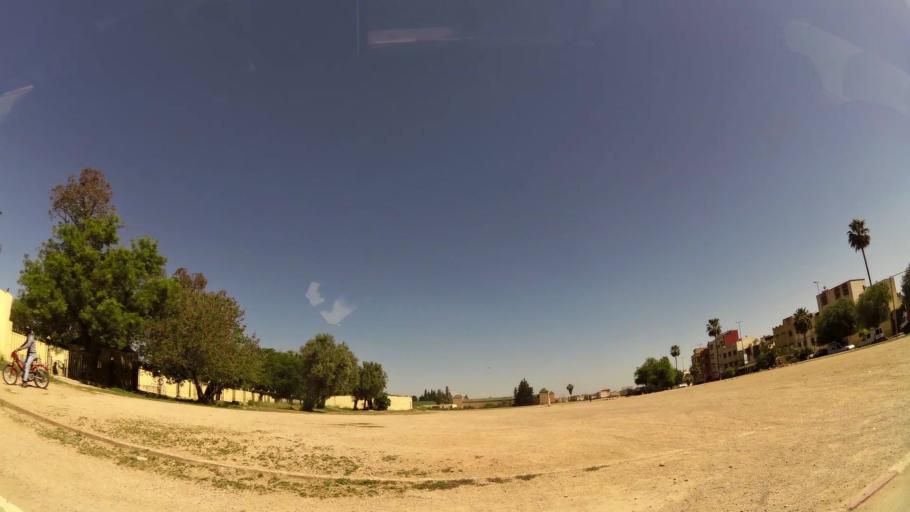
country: MA
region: Meknes-Tafilalet
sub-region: Meknes
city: Meknes
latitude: 33.8777
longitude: -5.5602
